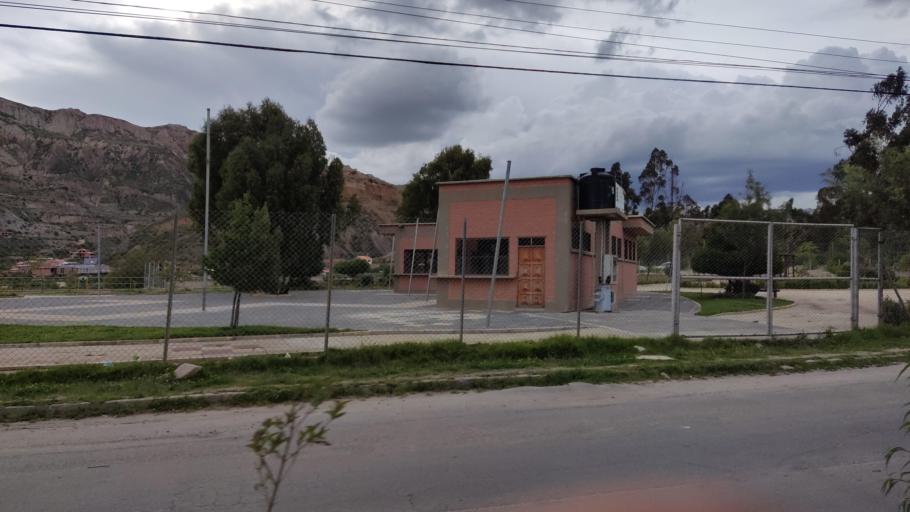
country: BO
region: La Paz
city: La Paz
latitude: -16.5777
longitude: -68.0808
